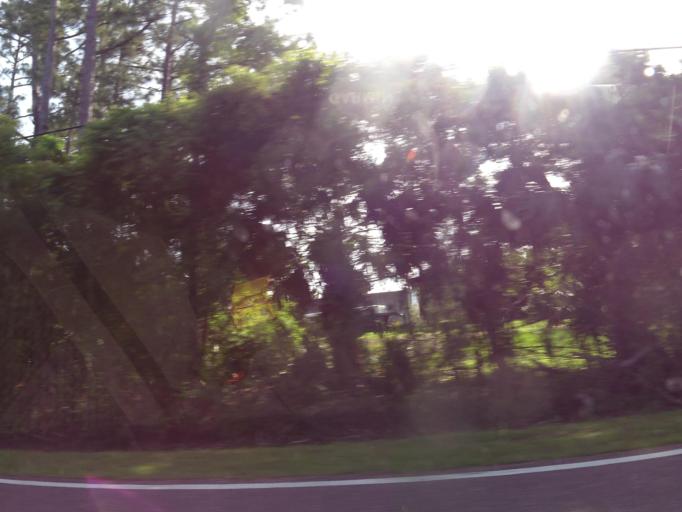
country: US
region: Florida
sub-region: Nassau County
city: Fernandina Beach
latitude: 30.5222
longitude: -81.4813
